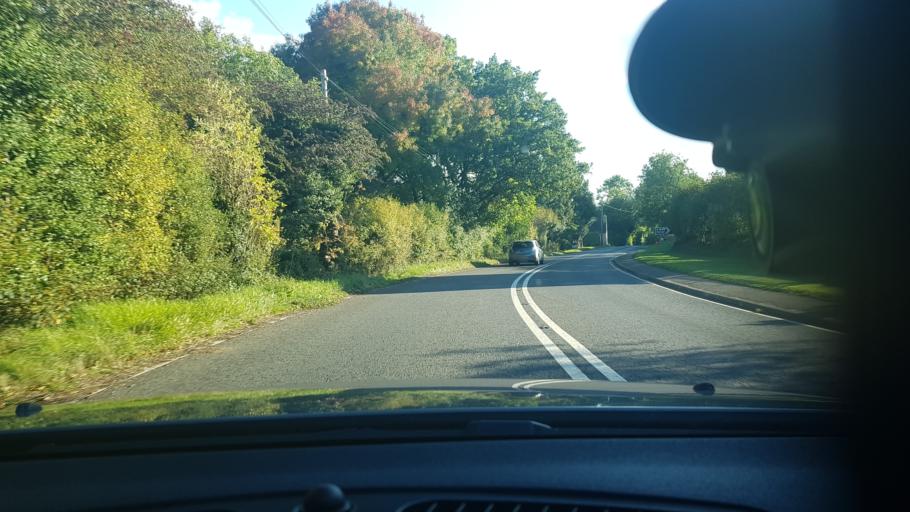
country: GB
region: England
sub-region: Gloucestershire
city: Cirencester
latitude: 51.7481
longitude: -1.9705
